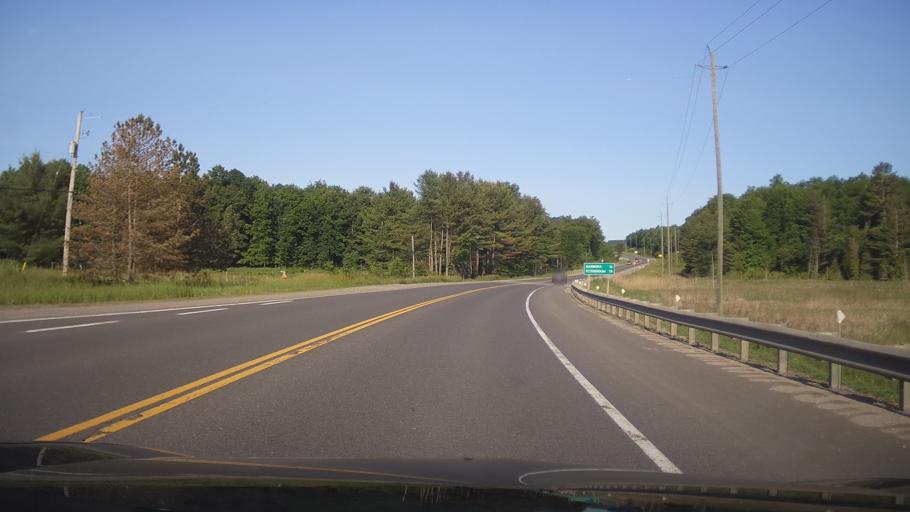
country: CA
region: Ontario
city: Quinte West
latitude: 44.5036
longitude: -77.5011
